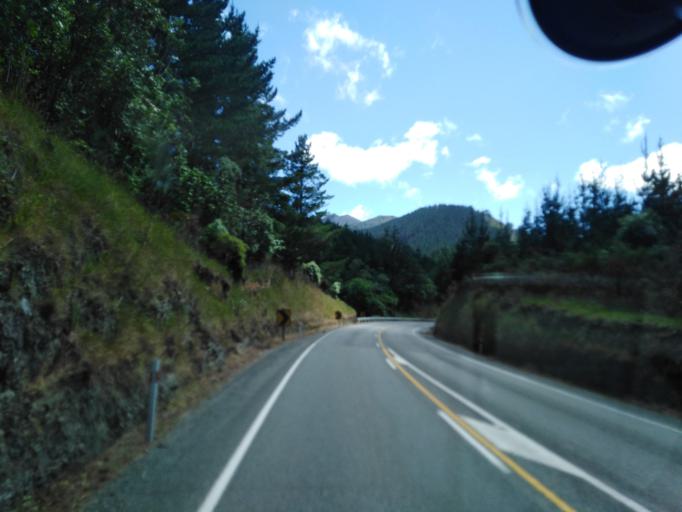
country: NZ
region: Nelson
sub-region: Nelson City
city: Nelson
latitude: -41.1772
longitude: 173.5608
